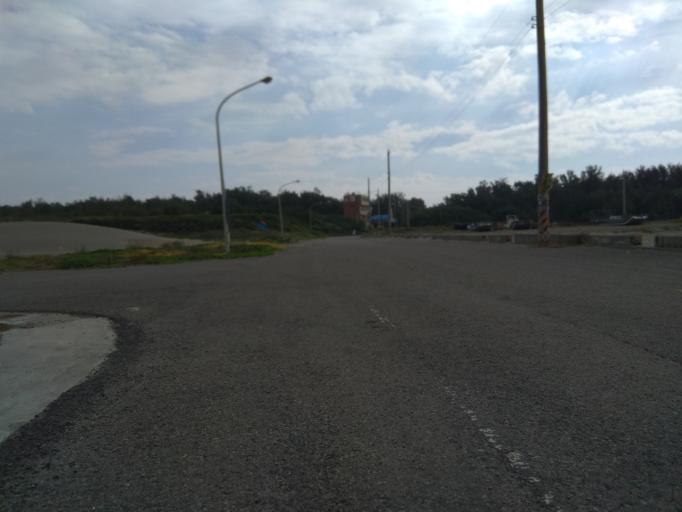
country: TW
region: Taiwan
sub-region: Hsinchu
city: Zhubei
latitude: 24.9268
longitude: 120.9726
